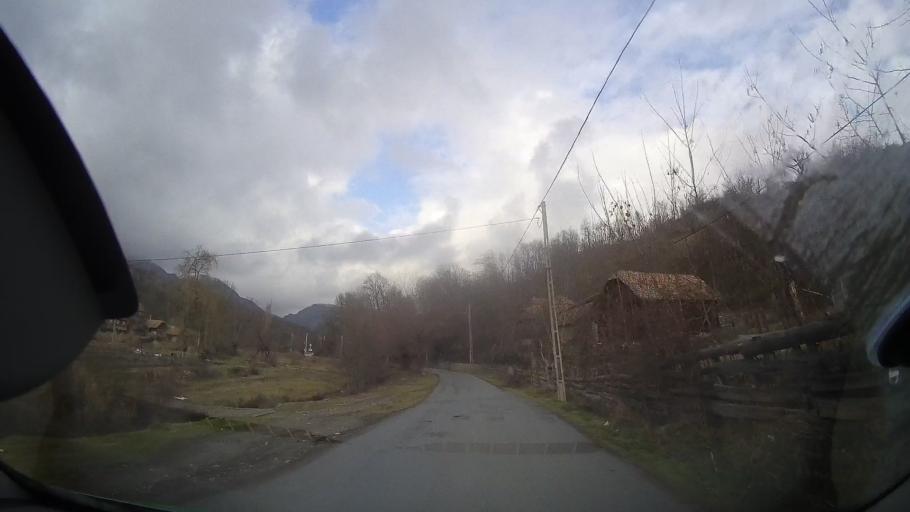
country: RO
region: Alba
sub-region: Comuna Ocolis
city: Ocolis
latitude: 46.4859
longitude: 23.4608
